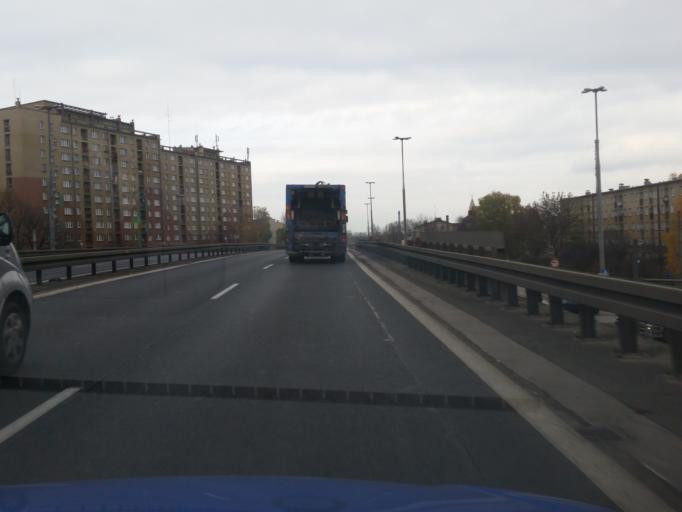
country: PL
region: Silesian Voivodeship
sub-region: Czestochowa
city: Czestochowa
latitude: 50.7841
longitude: 19.1431
